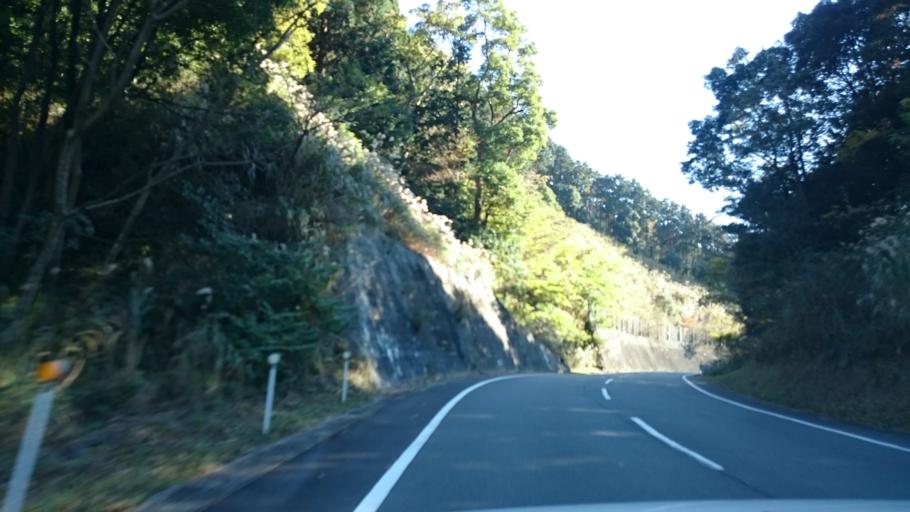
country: JP
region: Shizuoka
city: Heda
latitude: 34.9790
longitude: 138.8163
